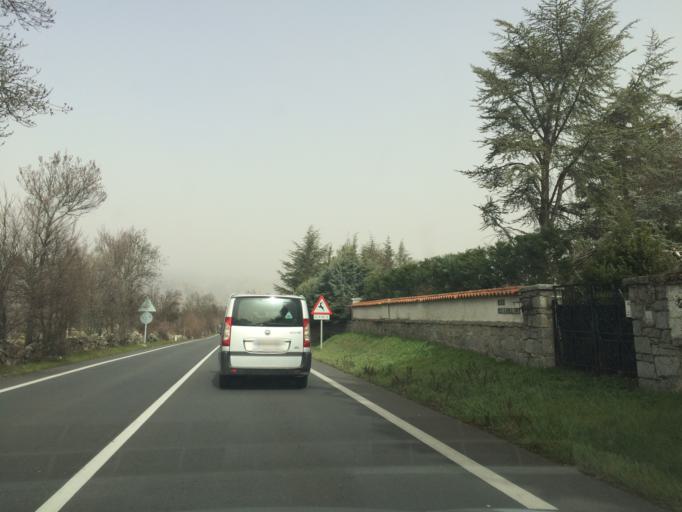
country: ES
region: Madrid
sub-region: Provincia de Madrid
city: Moralzarzal
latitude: 40.6813
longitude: -3.9567
